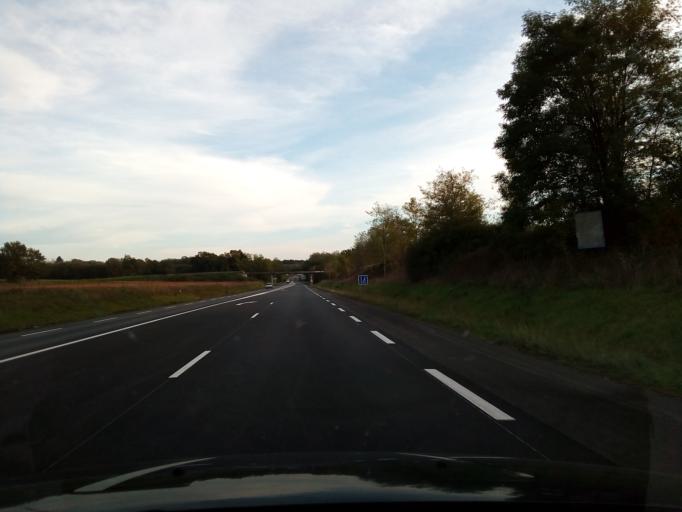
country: FR
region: Poitou-Charentes
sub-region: Departement de la Charente
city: Chasseneuil-sur-Bonnieure
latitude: 45.8371
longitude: 0.4640
